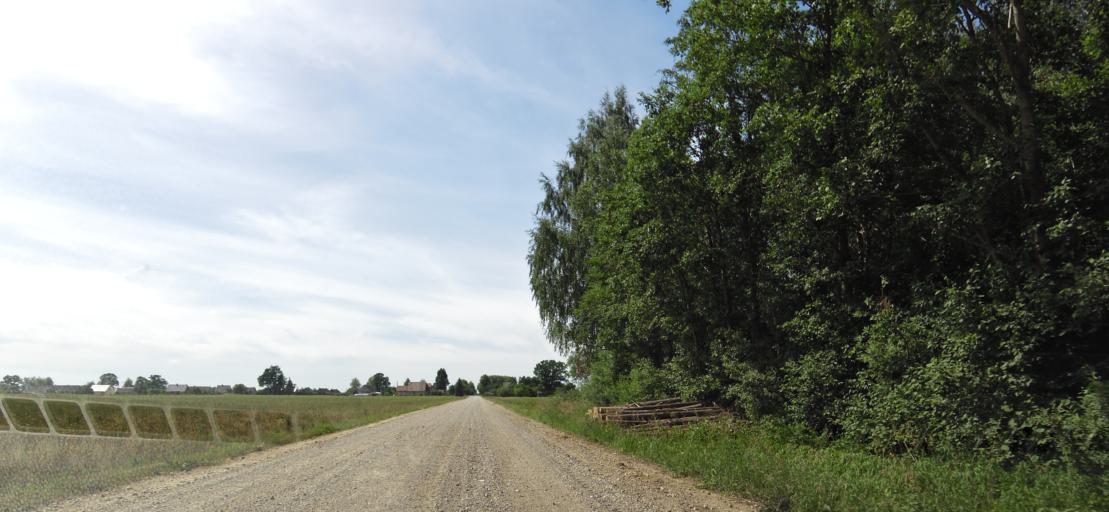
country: LT
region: Panevezys
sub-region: Panevezys City
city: Panevezys
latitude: 55.8820
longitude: 24.3088
